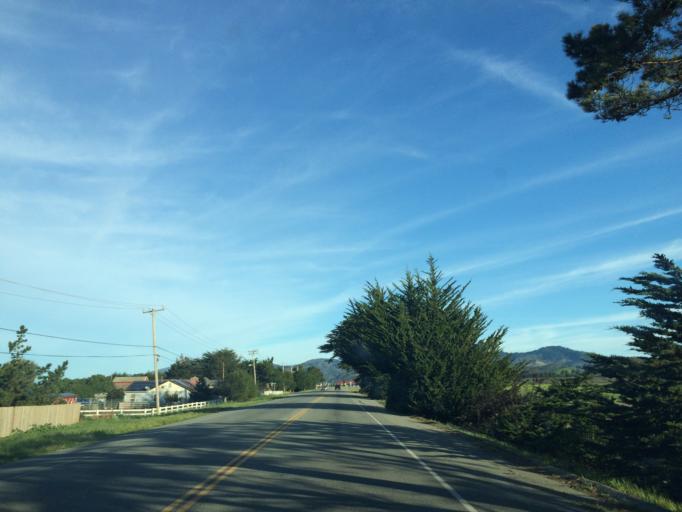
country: US
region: California
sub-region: San Mateo County
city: Half Moon Bay
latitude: 37.4426
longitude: -122.4282
